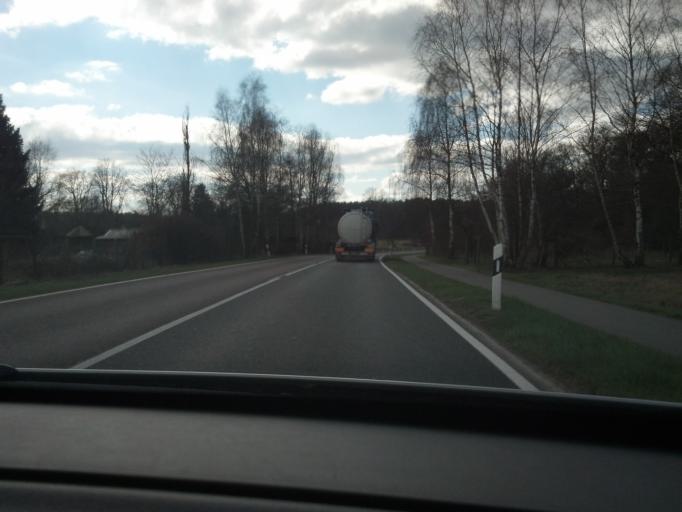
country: DE
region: Mecklenburg-Vorpommern
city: Wesenberg
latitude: 53.2705
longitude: 12.8997
